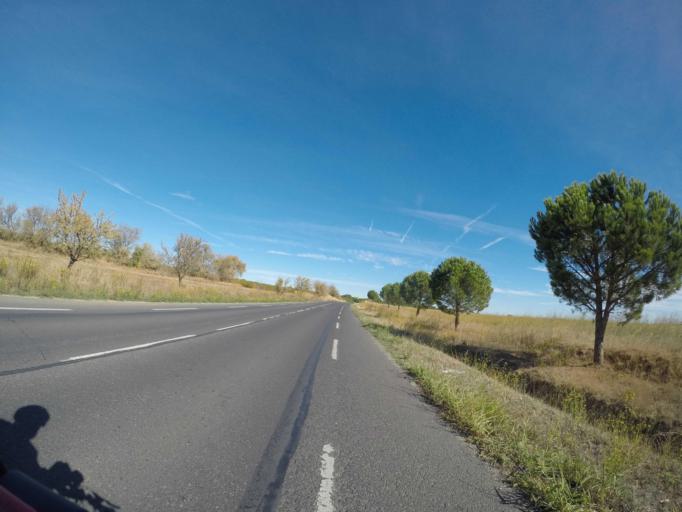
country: FR
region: Languedoc-Roussillon
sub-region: Departement des Pyrenees-Orientales
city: Ponteilla
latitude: 42.6194
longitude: 2.8111
